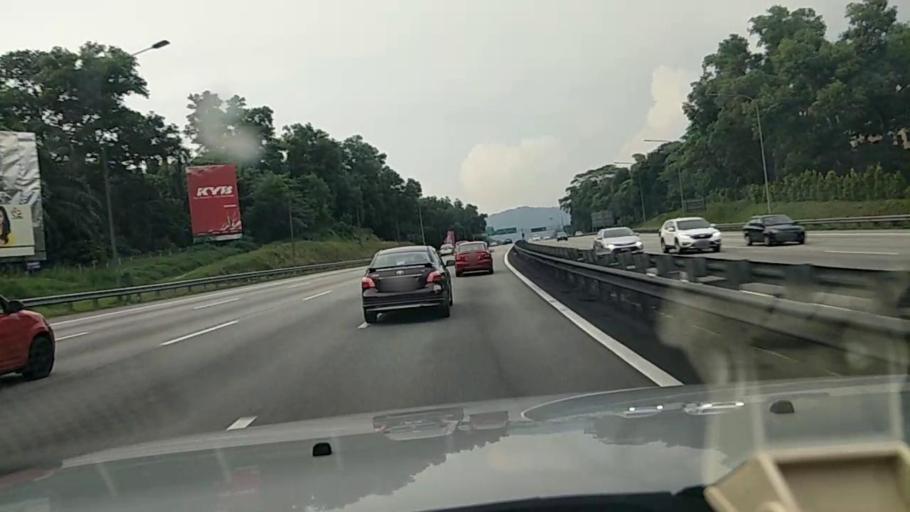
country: MY
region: Selangor
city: Kampung Baru Subang
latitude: 3.1932
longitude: 101.5825
